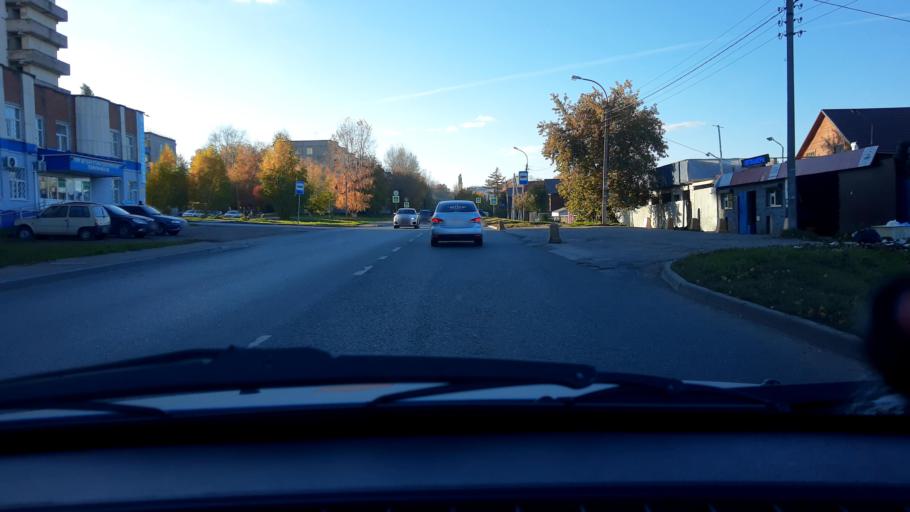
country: RU
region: Bashkortostan
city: Ufa
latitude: 54.8208
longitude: 56.1181
